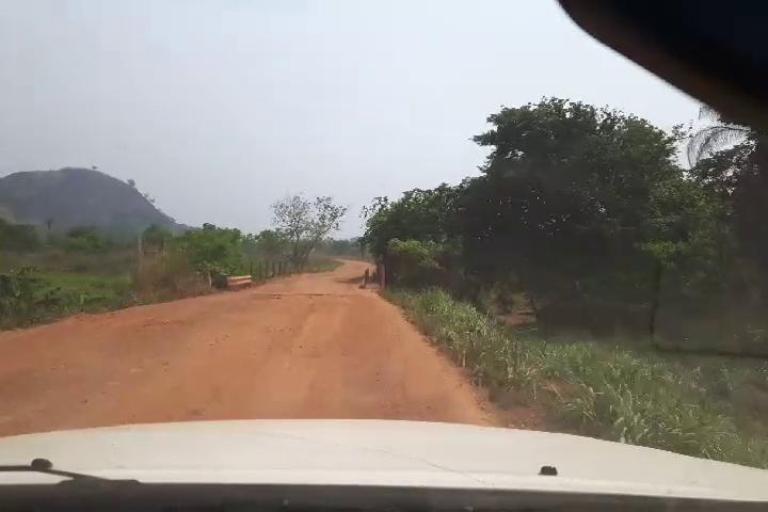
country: SL
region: Northern Province
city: Bumbuna
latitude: 8.9556
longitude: -11.8048
